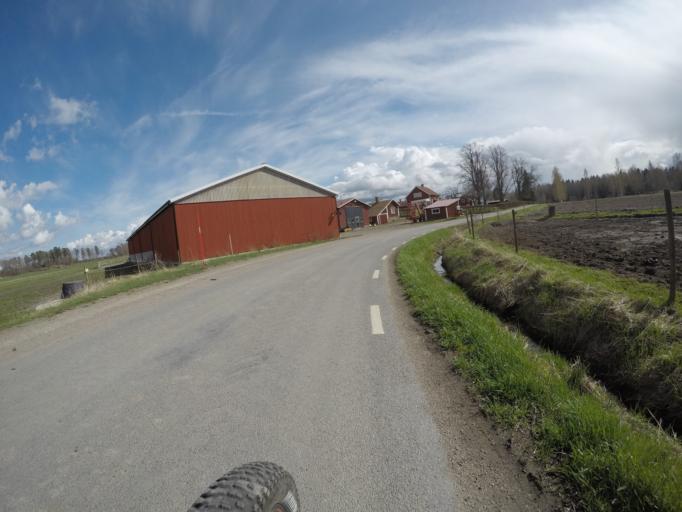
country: SE
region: Vaestmanland
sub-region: Kungsors Kommun
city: Kungsoer
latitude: 59.2984
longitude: 16.1411
